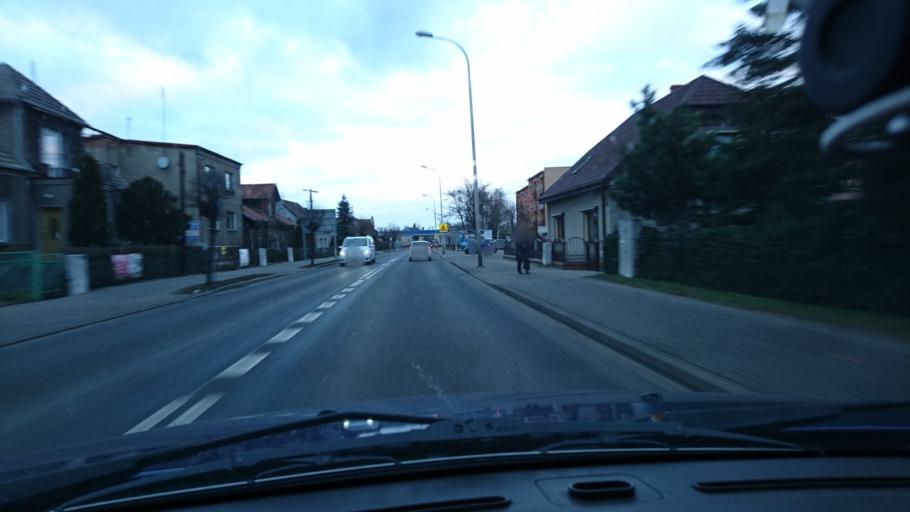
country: PL
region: Greater Poland Voivodeship
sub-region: Powiat kepinski
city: Kepno
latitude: 51.2862
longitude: 17.9930
